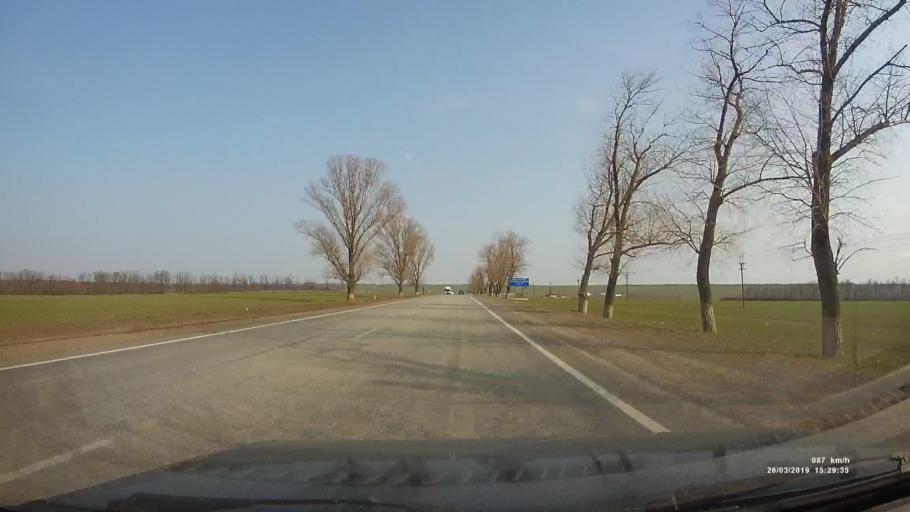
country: RU
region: Rostov
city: Primorka
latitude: 47.3148
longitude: 39.1022
